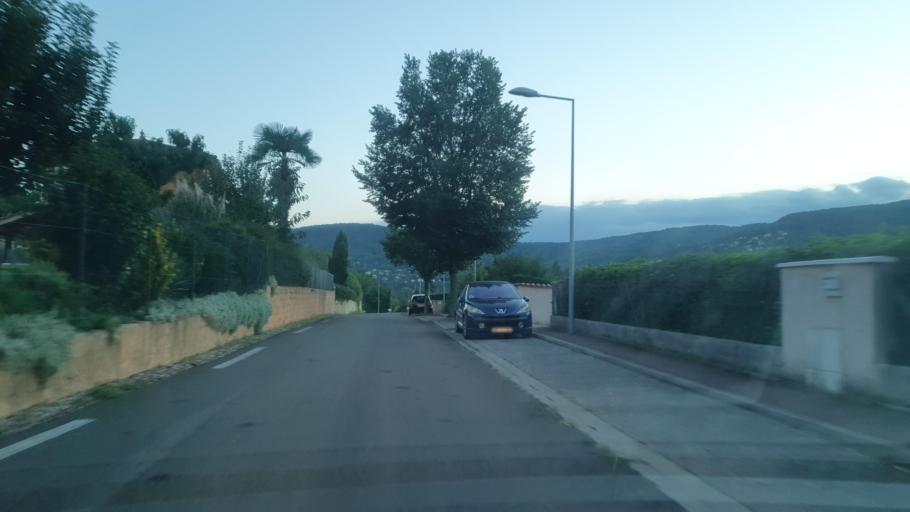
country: FR
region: Rhone-Alpes
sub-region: Departement du Rhone
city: Rochetaillee-sur-Saone
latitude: 45.8508
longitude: 4.8403
